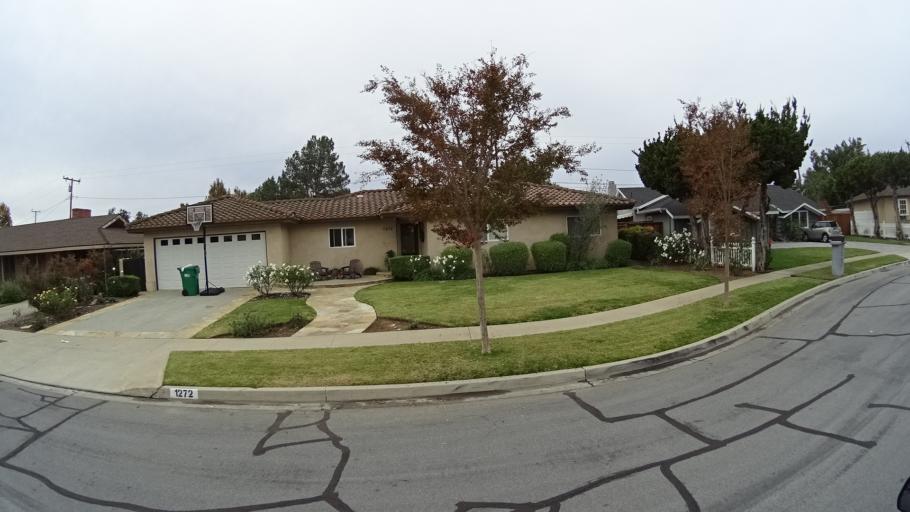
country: US
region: California
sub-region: Orange County
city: North Tustin
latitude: 33.7510
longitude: -117.8028
